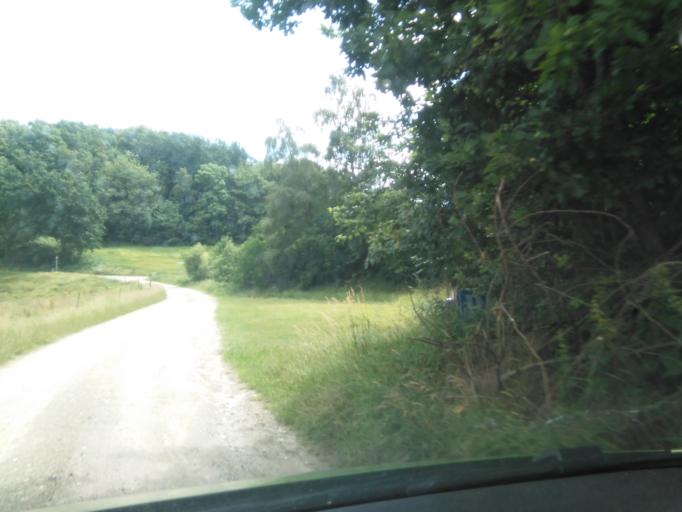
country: DK
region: Central Jutland
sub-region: Arhus Kommune
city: Logten
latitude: 56.1690
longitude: 10.4094
